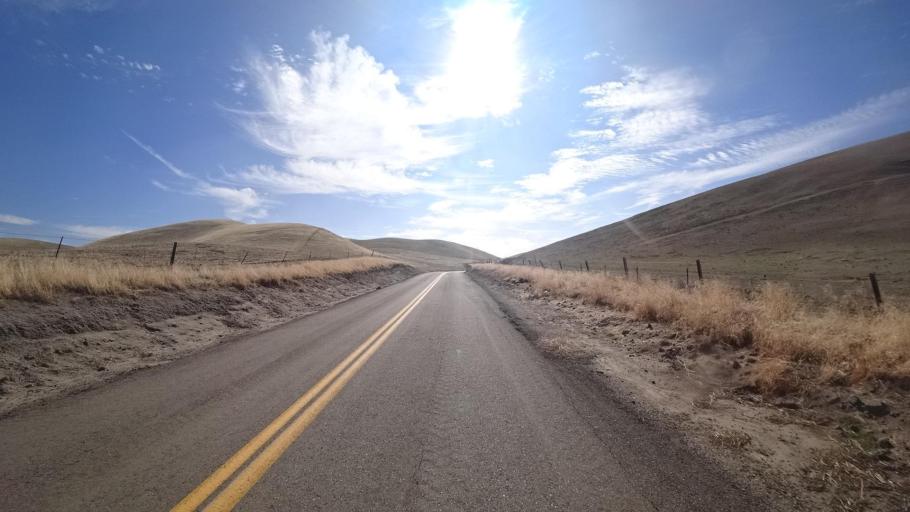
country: US
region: California
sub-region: Kern County
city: Oildale
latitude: 35.6212
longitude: -118.9412
